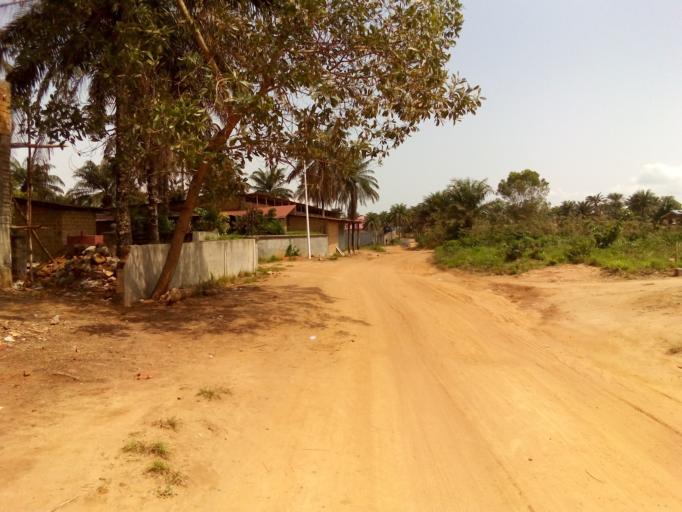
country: SL
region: Western Area
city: Waterloo
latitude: 8.3470
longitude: -13.0150
